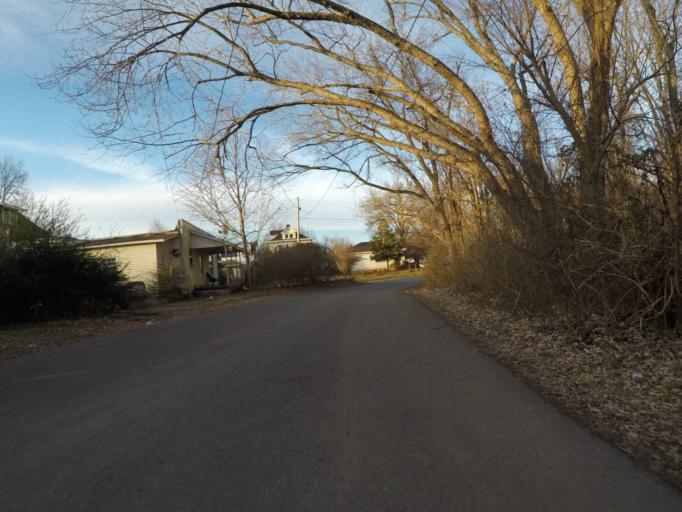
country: US
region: Ohio
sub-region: Lawrence County
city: Burlington
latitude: 38.4029
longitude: -82.4986
